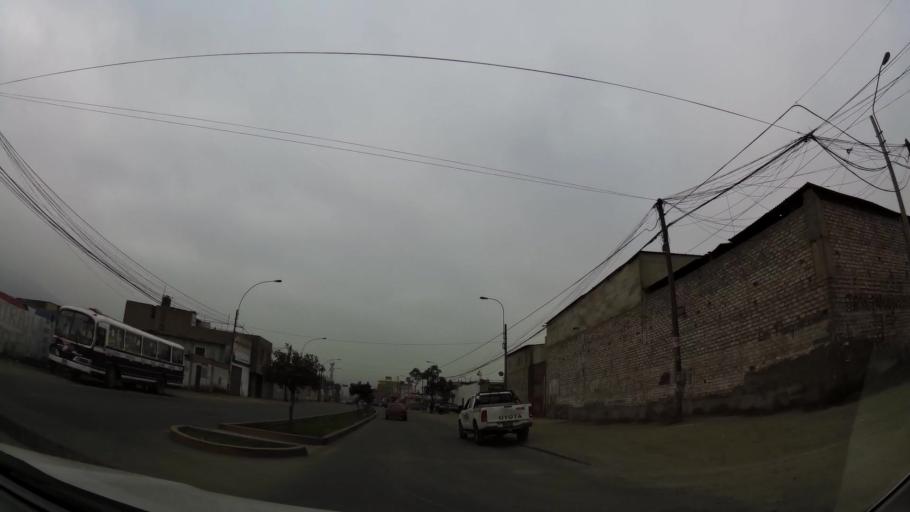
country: PE
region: Lima
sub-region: Lima
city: Independencia
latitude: -11.9802
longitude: -76.9920
